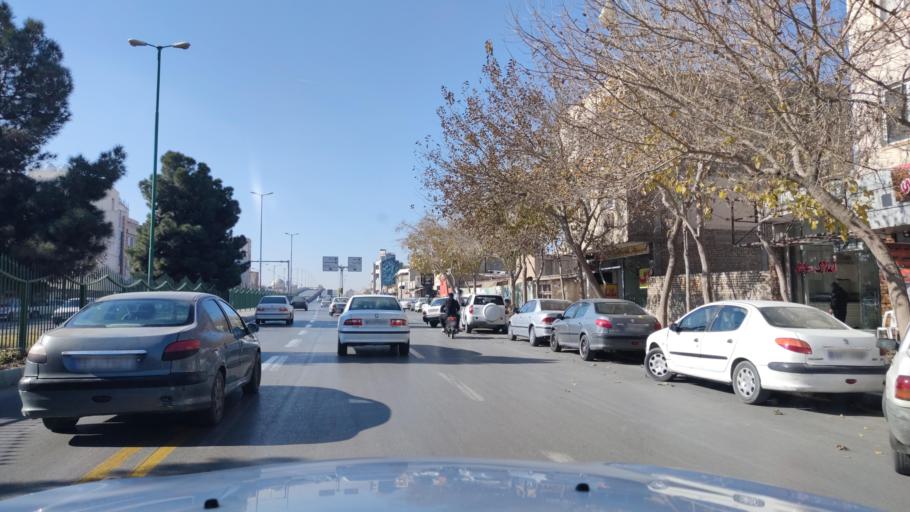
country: IR
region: Isfahan
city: Isfahan
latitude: 32.6790
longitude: 51.6765
